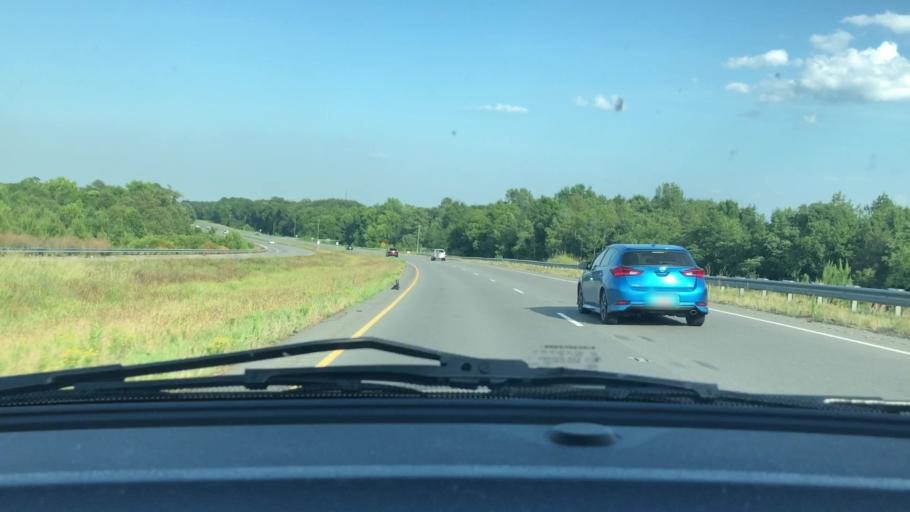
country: US
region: North Carolina
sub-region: Chatham County
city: Farmville
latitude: 35.5579
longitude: -79.2912
